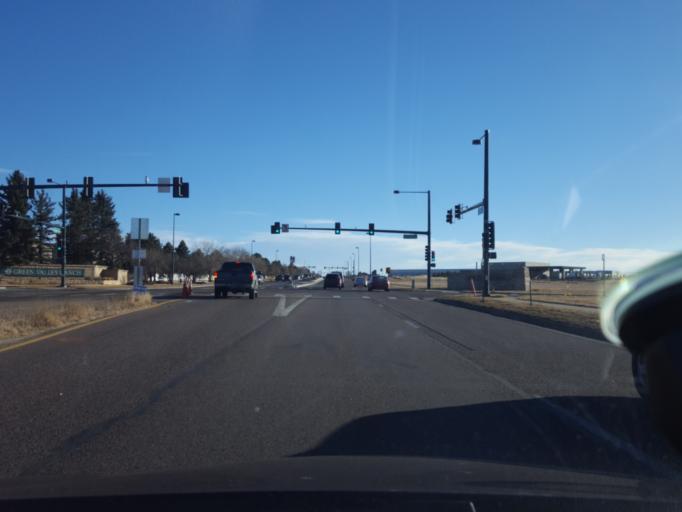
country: US
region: Colorado
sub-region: Adams County
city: Aurora
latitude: 39.7786
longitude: -104.7722
